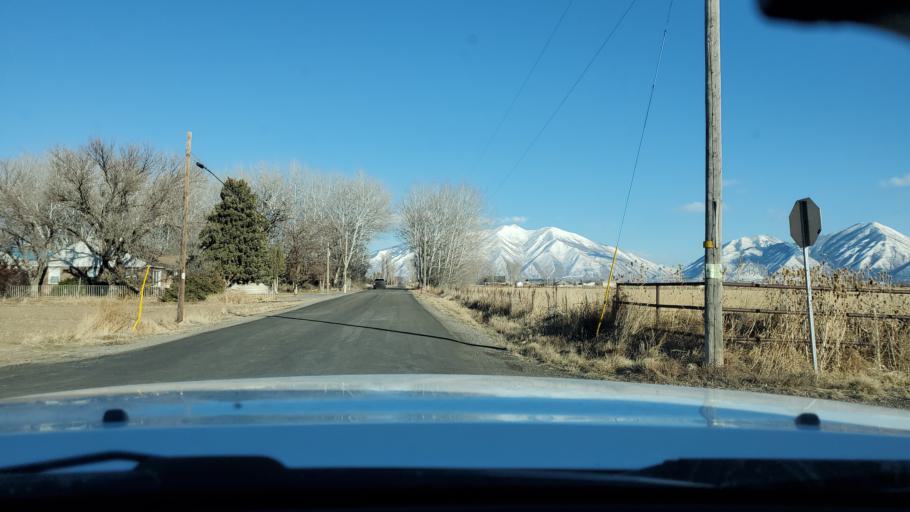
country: US
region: Utah
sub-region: Utah County
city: Benjamin
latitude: 40.1146
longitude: -111.7499
